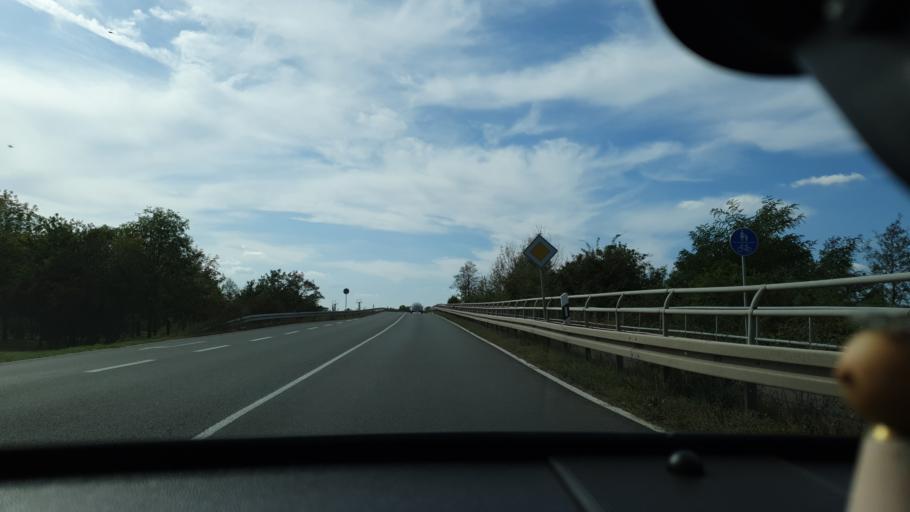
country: DE
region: Saxony
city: Jesewitz
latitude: 51.4587
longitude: 12.5854
